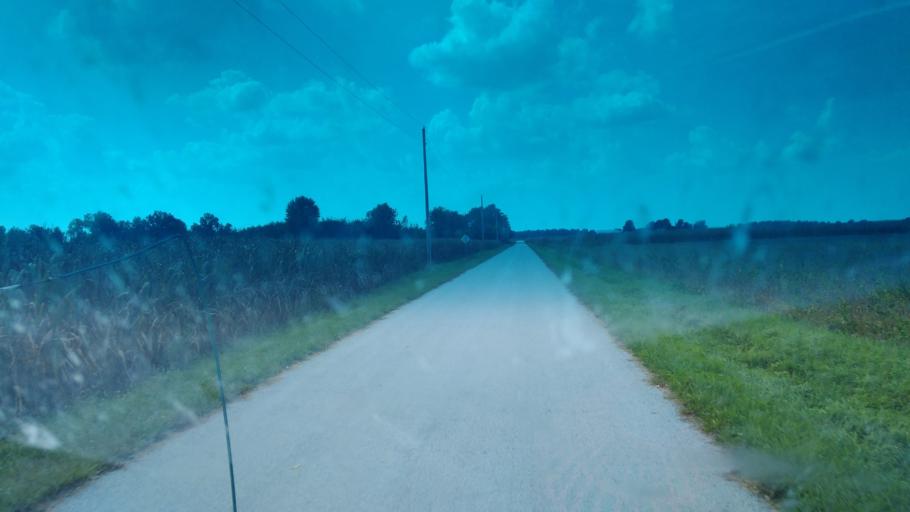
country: US
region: Ohio
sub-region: Hardin County
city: Kenton
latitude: 40.6894
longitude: -83.7211
